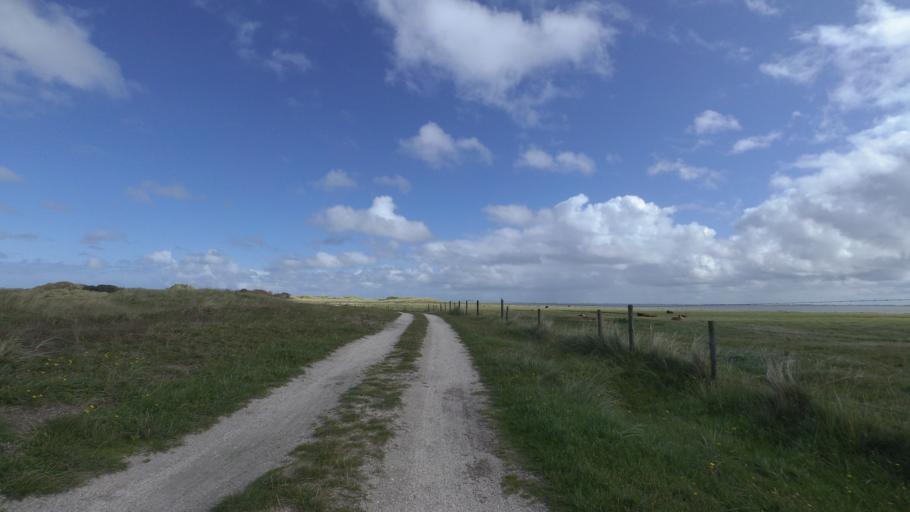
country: NL
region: Friesland
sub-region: Gemeente Ameland
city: Nes
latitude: 53.4473
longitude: 5.8558
